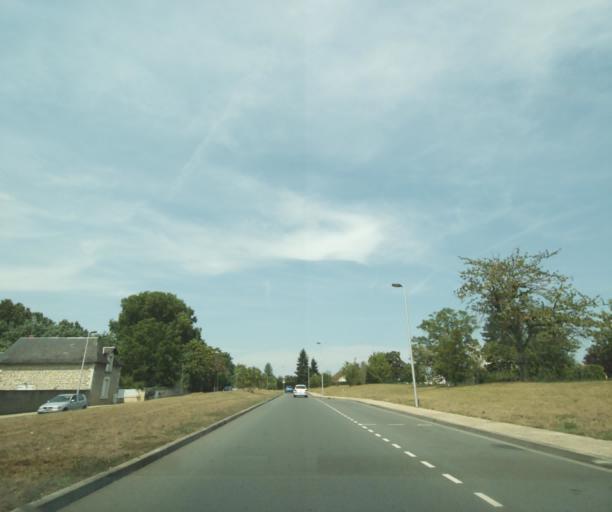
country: FR
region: Poitou-Charentes
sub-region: Departement de la Vienne
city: Antran
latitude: 46.8778
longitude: 0.5661
